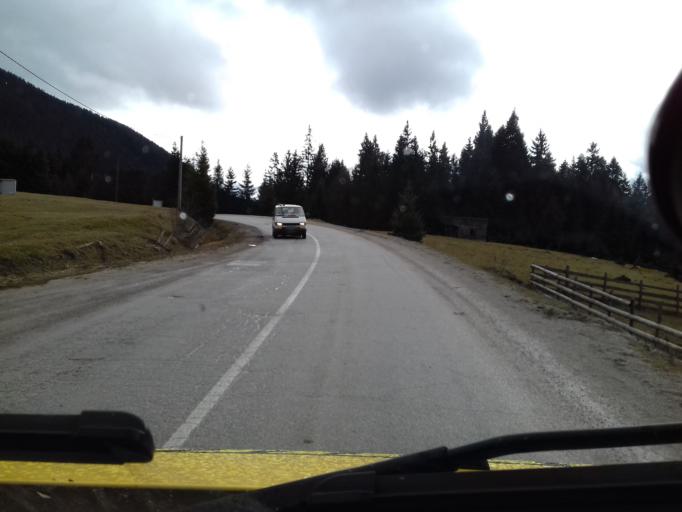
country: BA
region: Federation of Bosnia and Herzegovina
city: Turbe
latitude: 44.3020
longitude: 17.4933
